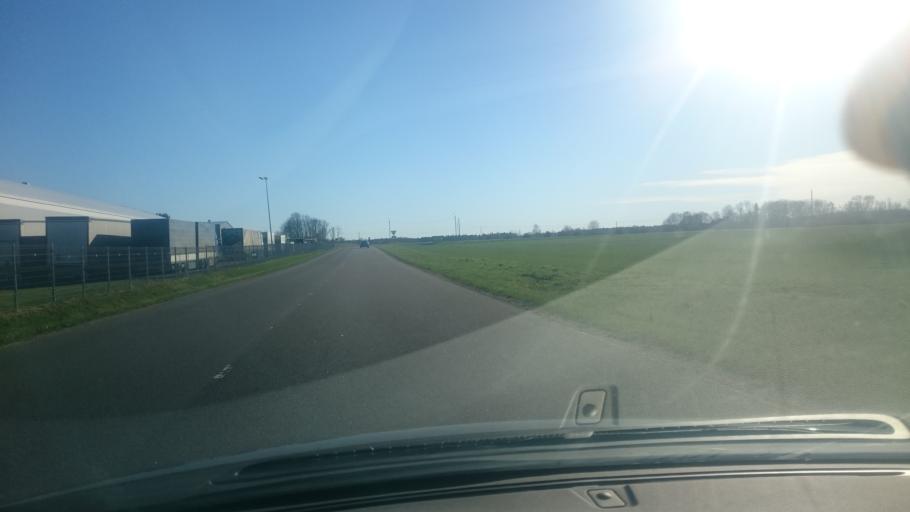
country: EE
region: Harju
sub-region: Kiili vald
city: Kiili
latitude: 59.3399
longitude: 24.8164
